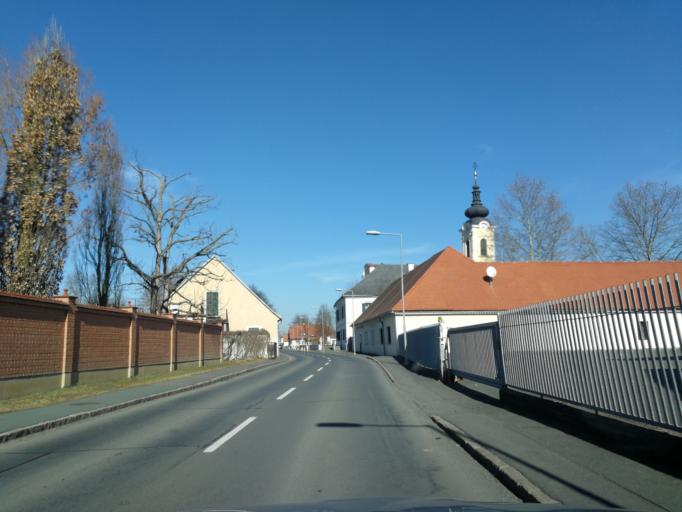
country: AT
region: Styria
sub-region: Politischer Bezirk Suedoststeiermark
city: Mureck
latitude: 46.7084
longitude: 15.7693
